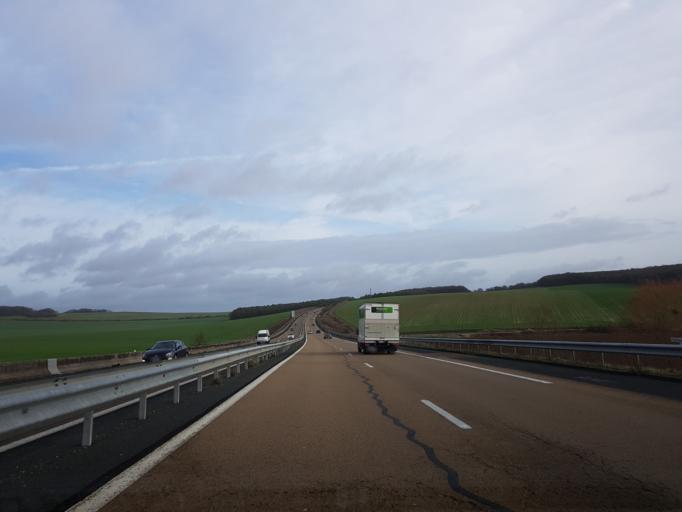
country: FR
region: Champagne-Ardenne
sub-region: Departement de l'Aube
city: Aix-en-Othe
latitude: 48.2610
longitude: 3.6762
